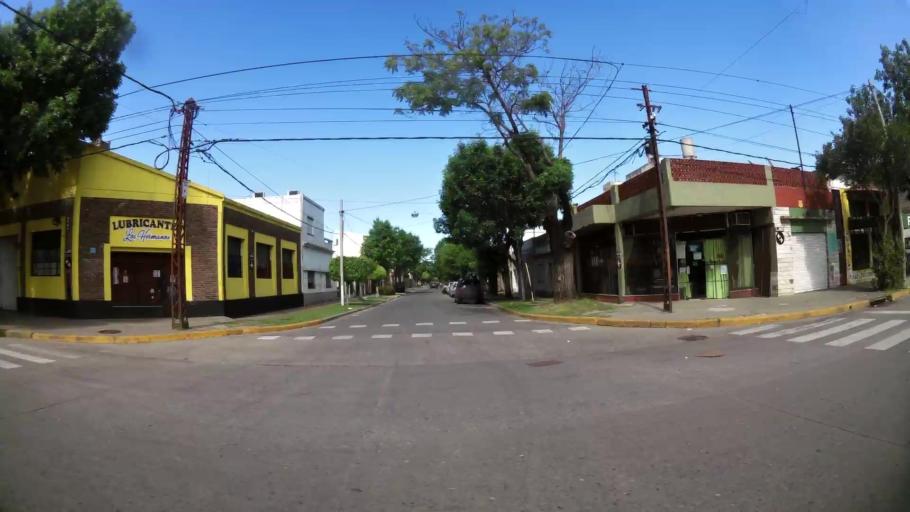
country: AR
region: Santa Fe
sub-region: Departamento de Rosario
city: Rosario
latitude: -32.9369
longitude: -60.7128
